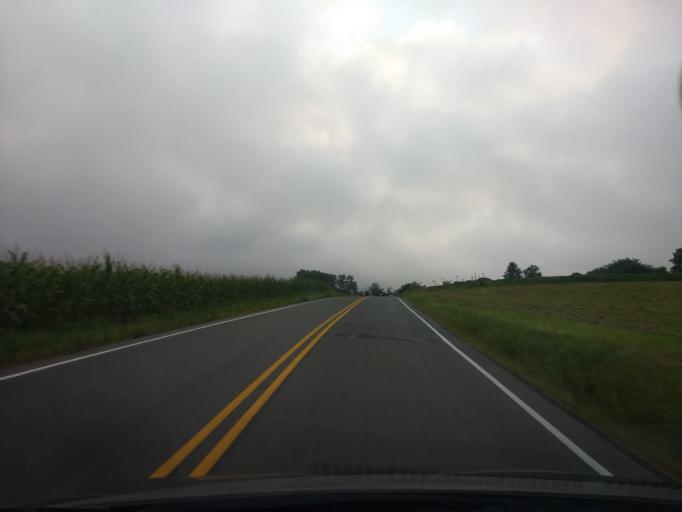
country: US
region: Pennsylvania
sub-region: Westmoreland County
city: Greensburg
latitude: 40.3405
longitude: -79.4955
